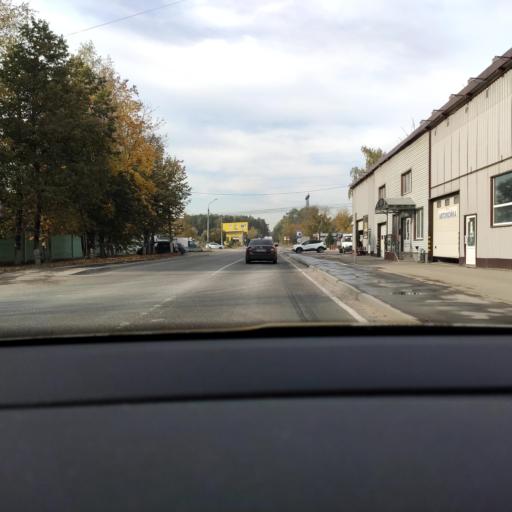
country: RU
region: Moskovskaya
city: Lesnyye Polyany
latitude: 55.9672
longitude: 37.8903
